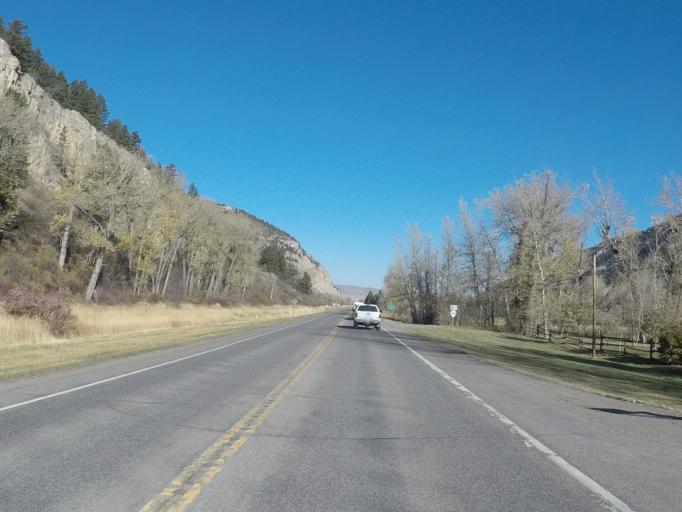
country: US
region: Montana
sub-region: Park County
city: Livingston
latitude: 45.5959
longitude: -110.5713
